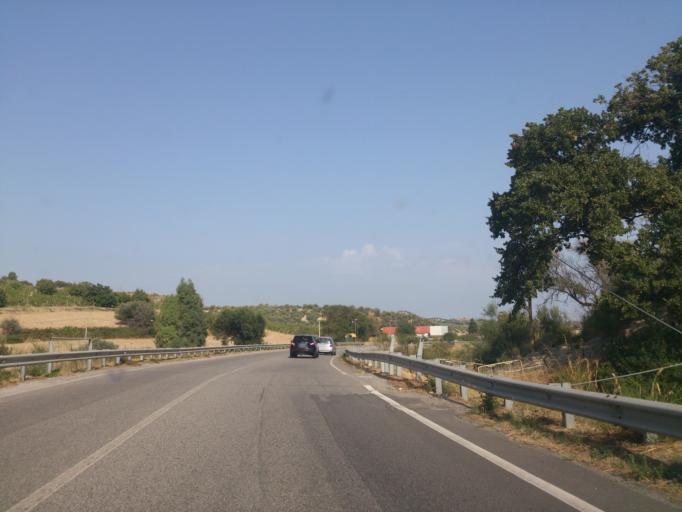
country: IT
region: Calabria
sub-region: Provincia di Reggio Calabria
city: Stilo
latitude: 38.4659
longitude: 16.4936
